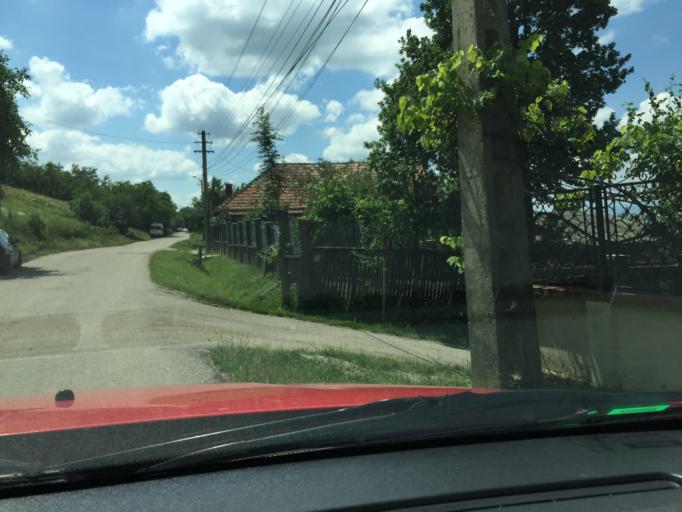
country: RO
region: Cluj
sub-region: Comuna Baciu
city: Baciu
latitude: 46.8206
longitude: 23.5348
